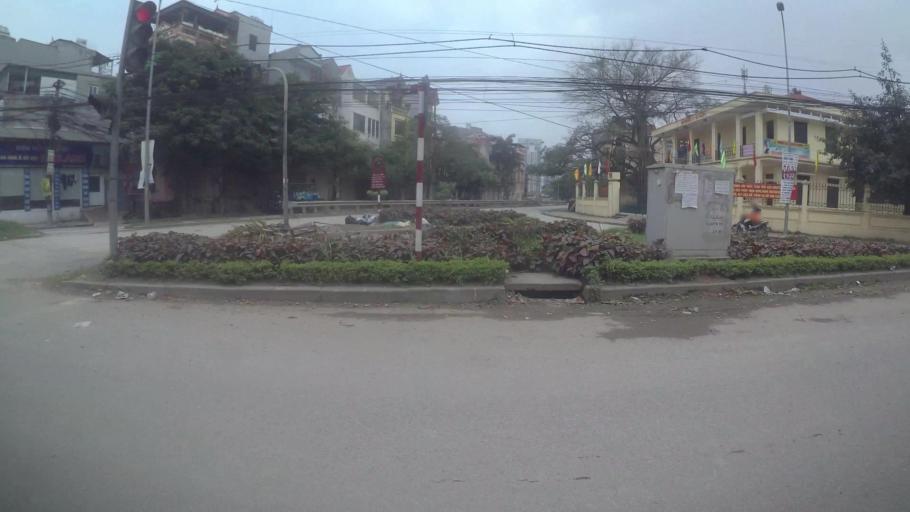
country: VN
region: Ha Noi
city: Tay Ho
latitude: 21.0812
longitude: 105.7854
